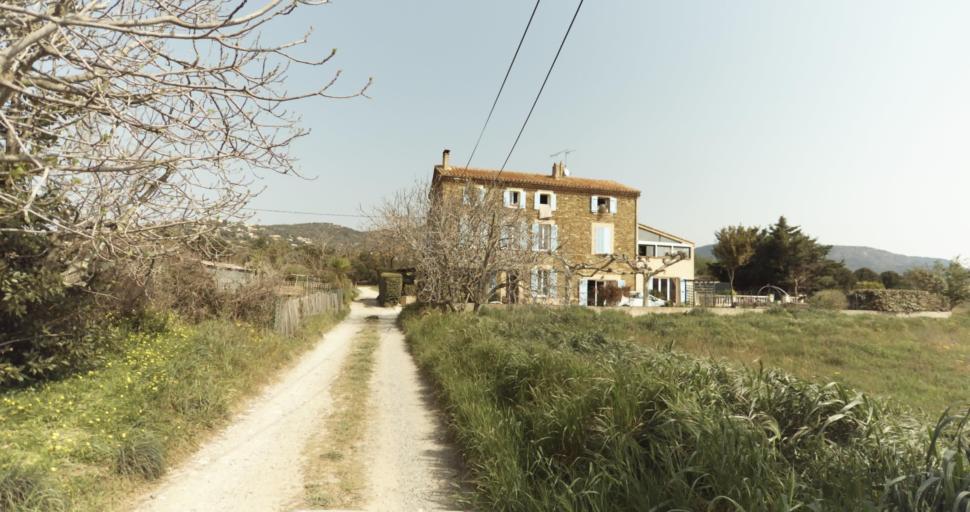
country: FR
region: Provence-Alpes-Cote d'Azur
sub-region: Departement du Var
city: Bormes-les-Mimosas
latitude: 43.1378
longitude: 6.3341
